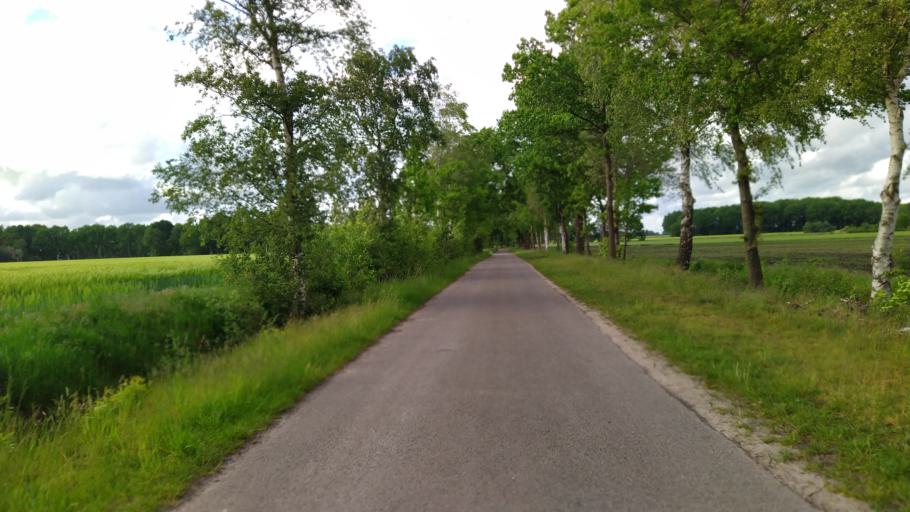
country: DE
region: Lower Saxony
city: Kutenholz
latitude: 53.4659
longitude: 9.3202
